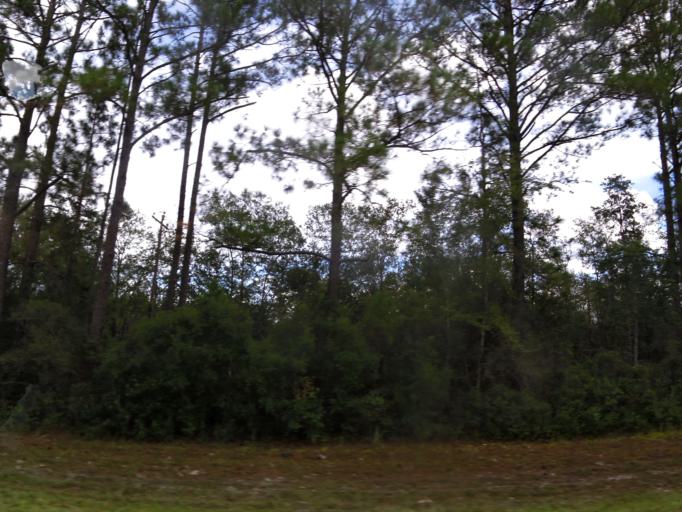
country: US
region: Georgia
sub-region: Brantley County
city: Nahunta
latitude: 31.1760
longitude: -81.9887
